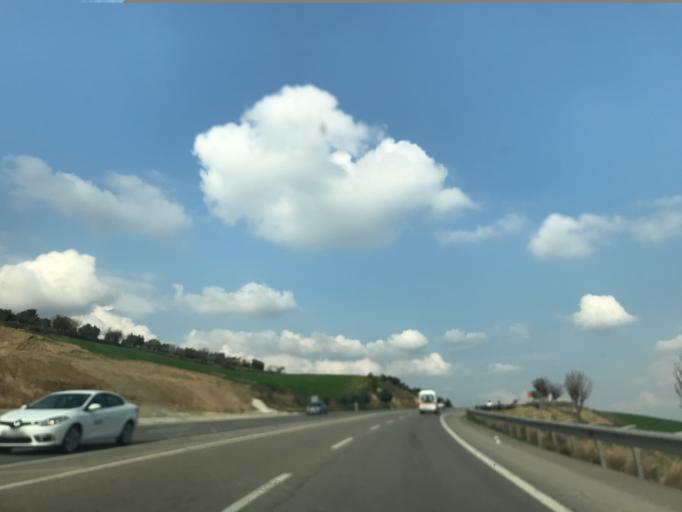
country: TR
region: Hatay
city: Kirikhan
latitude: 36.4611
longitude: 36.2793
